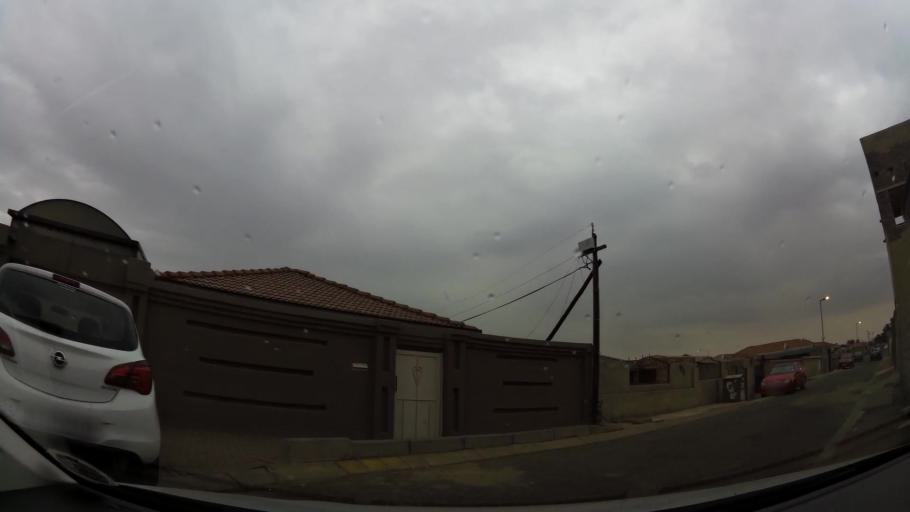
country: ZA
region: Gauteng
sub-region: City of Johannesburg Metropolitan Municipality
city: Soweto
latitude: -26.2525
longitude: 27.8657
